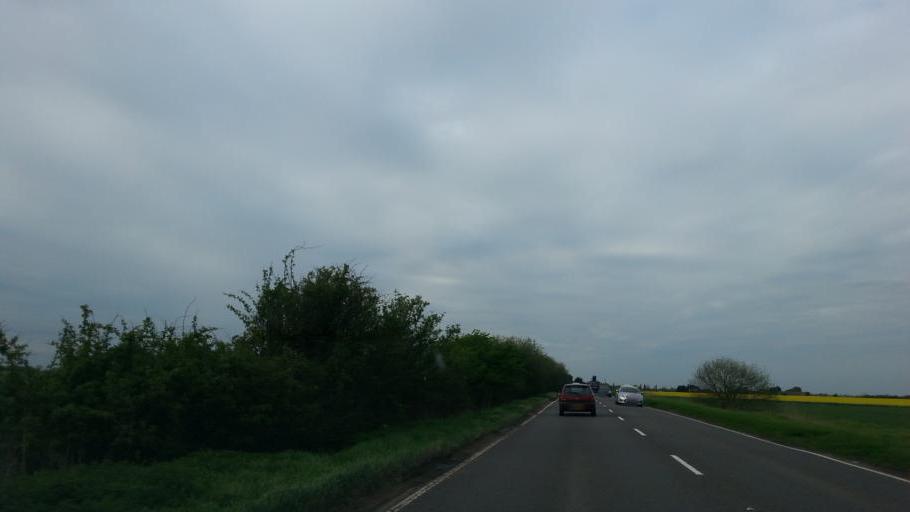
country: GB
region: England
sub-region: Cambridgeshire
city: March
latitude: 52.5791
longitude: 0.0563
